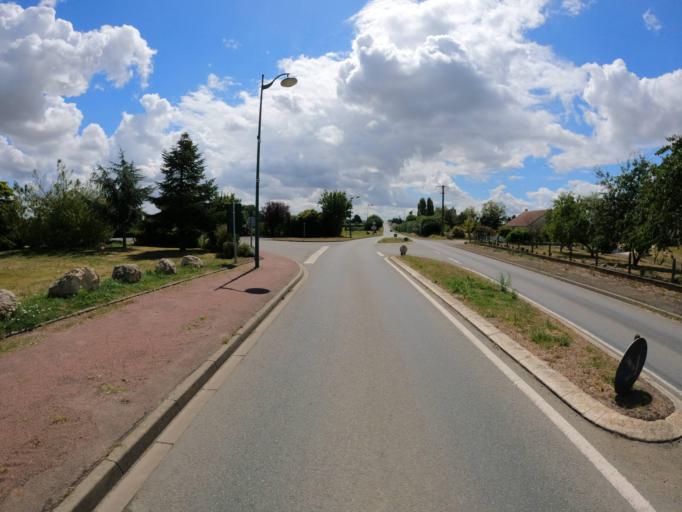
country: FR
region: Pays de la Loire
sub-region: Departement de la Sarthe
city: Juigne-sur-Sarthe
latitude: 47.9169
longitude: -0.2678
